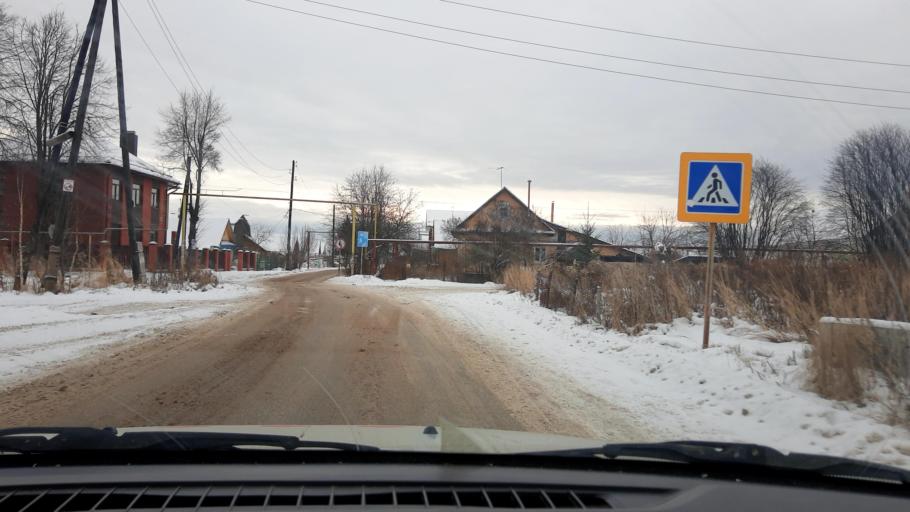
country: RU
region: Nizjnij Novgorod
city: Gorodets
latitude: 56.6682
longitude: 43.4769
